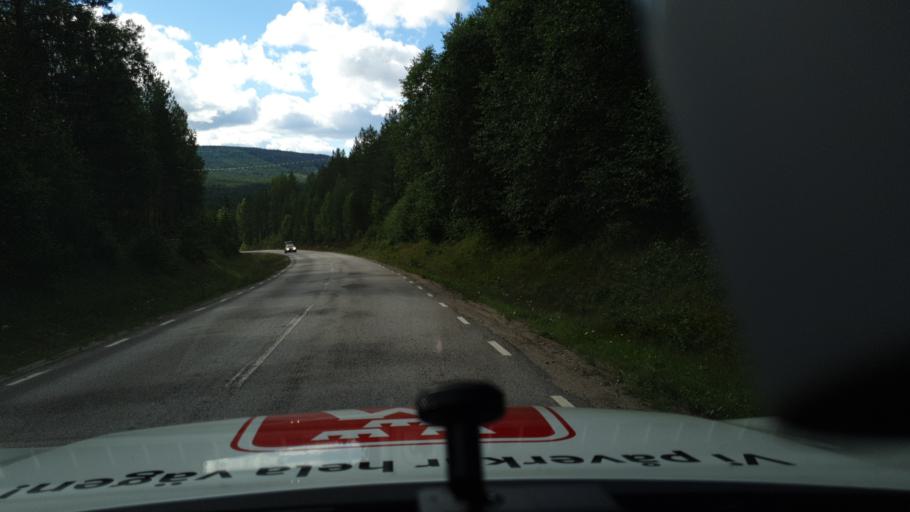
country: NO
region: Hedmark
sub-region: Trysil
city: Innbygda
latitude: 61.0303
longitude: 12.4807
